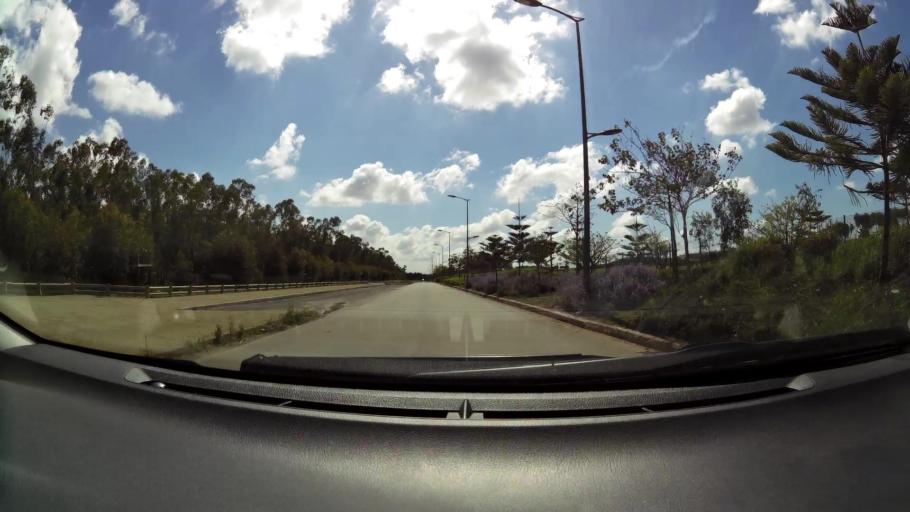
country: MA
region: Grand Casablanca
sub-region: Nouaceur
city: Bouskoura
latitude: 33.4797
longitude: -7.5895
